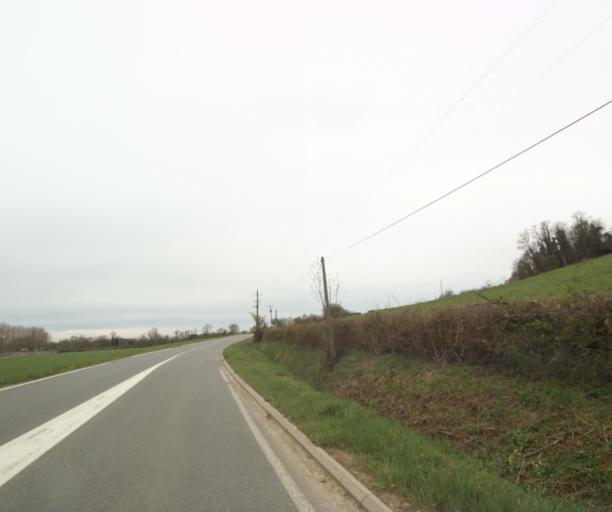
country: FR
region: Bourgogne
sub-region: Departement de Saone-et-Loire
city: Charnay-les-Macon
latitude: 46.2966
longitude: 4.7675
